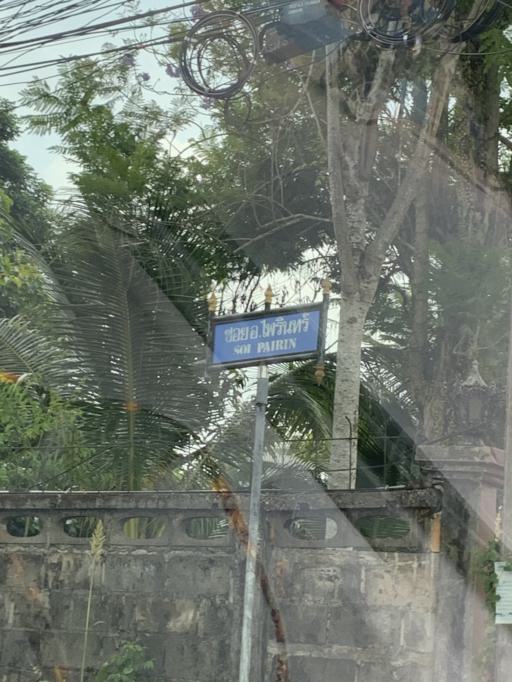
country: TH
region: Yala
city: Yala
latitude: 6.5317
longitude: 101.2928
